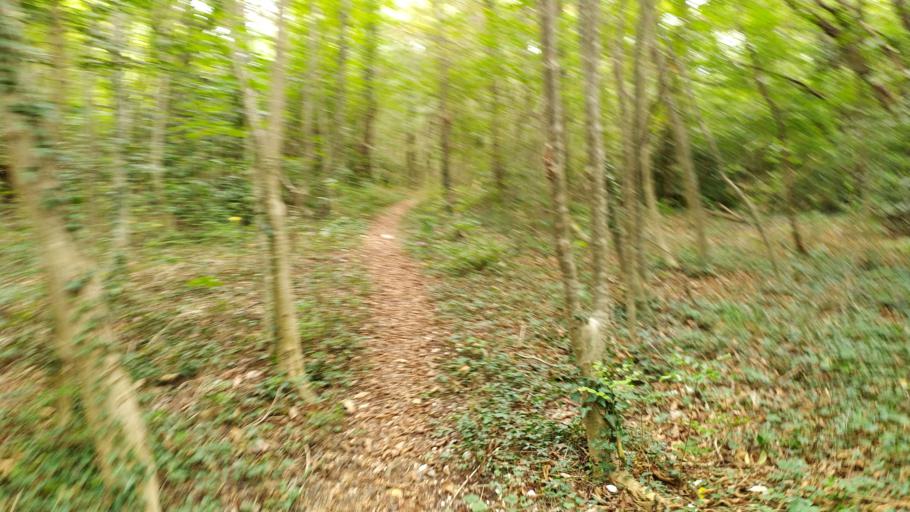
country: IT
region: Friuli Venezia Giulia
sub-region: Provincia di Pordenone
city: Aviano-Castello
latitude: 46.0732
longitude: 12.5734
